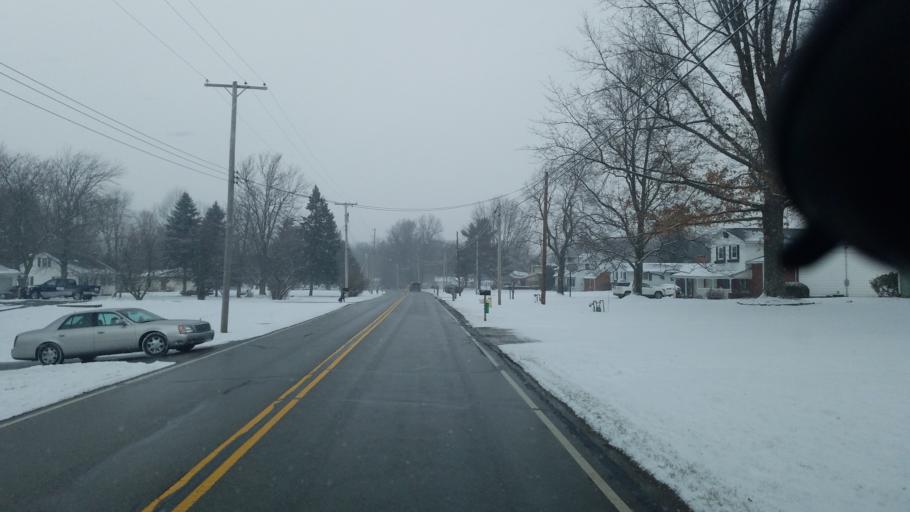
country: US
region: Ohio
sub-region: Richland County
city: Ontario
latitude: 40.7719
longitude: -82.6479
